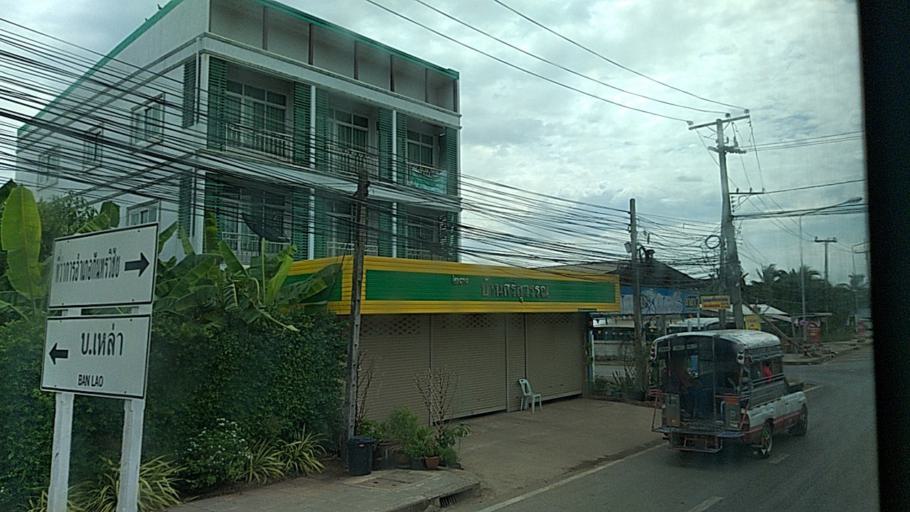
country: TH
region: Maha Sarakham
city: Kantharawichai
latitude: 16.3217
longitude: 103.2991
